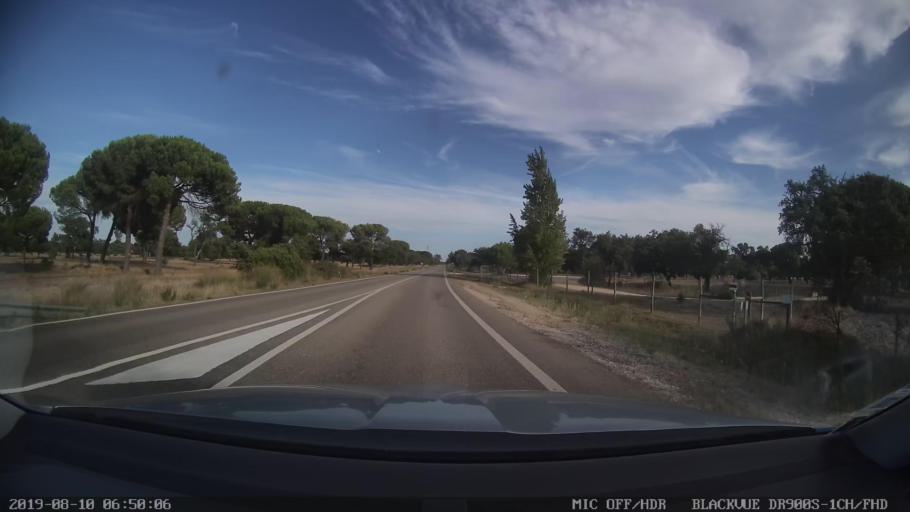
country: PT
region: Santarem
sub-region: Benavente
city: Benavente
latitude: 38.9101
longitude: -8.7639
